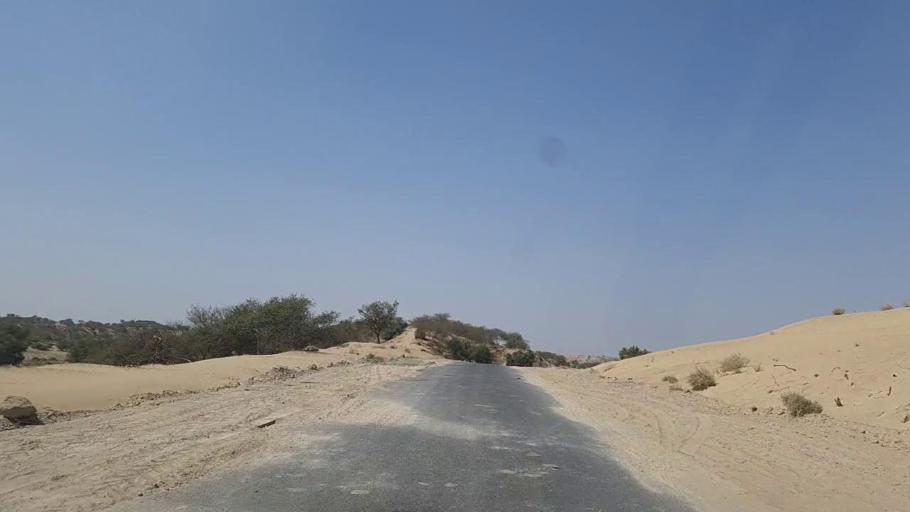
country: PK
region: Sindh
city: Diplo
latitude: 24.5870
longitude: 69.5373
